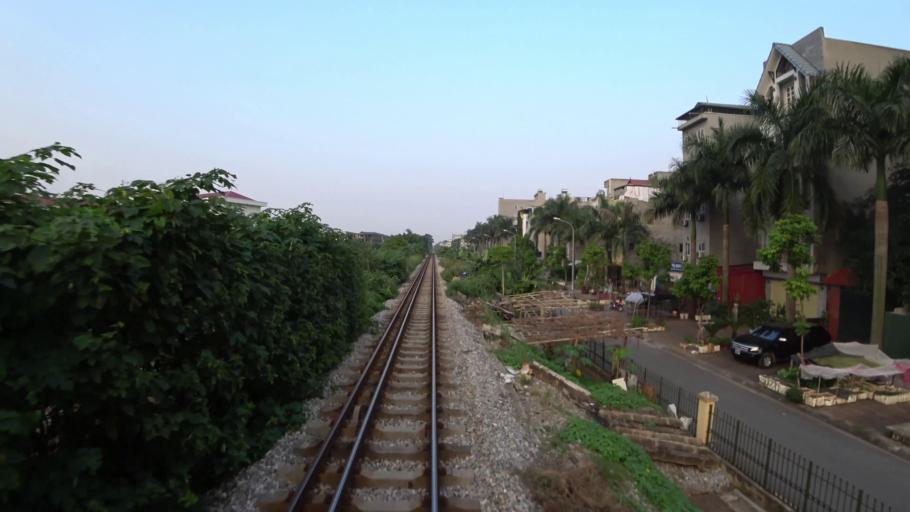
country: VN
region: Ha Noi
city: Trau Quy
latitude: 21.0761
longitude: 105.9071
